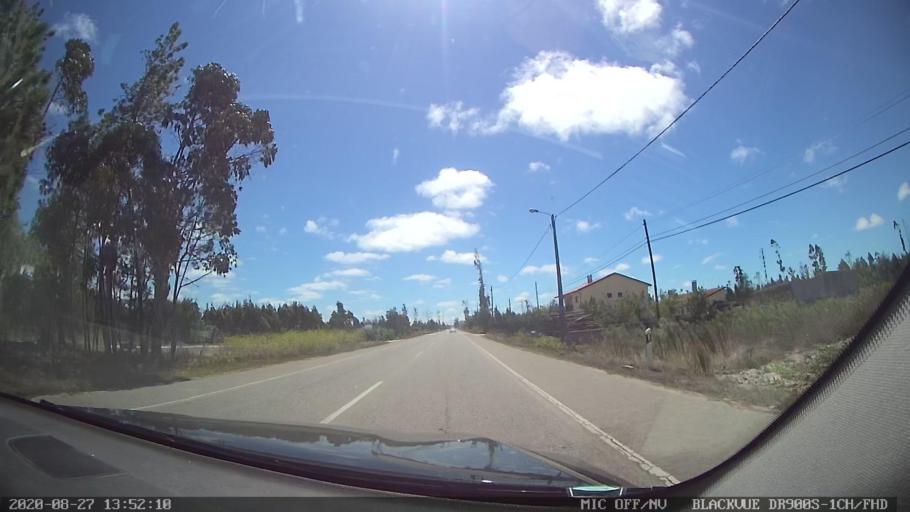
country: PT
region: Coimbra
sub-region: Mira
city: Mira
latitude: 40.3416
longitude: -8.7497
